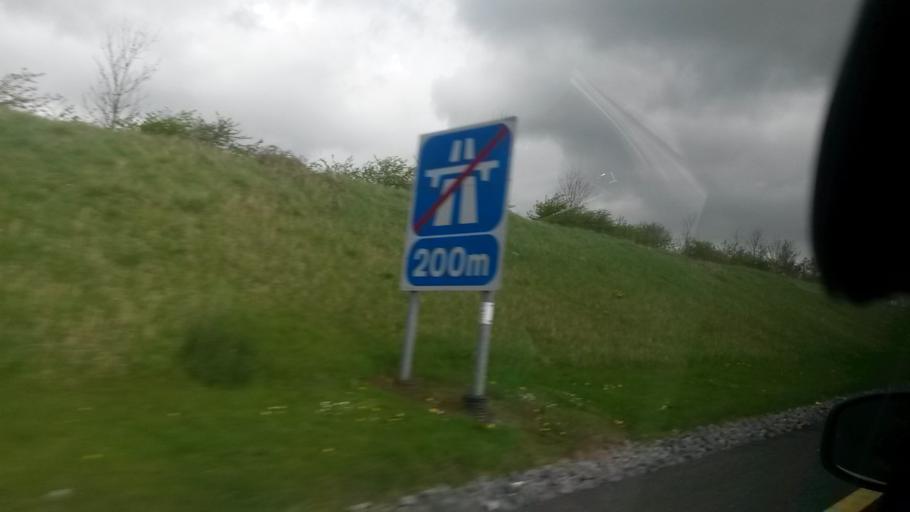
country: IE
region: Munster
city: Cashel
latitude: 52.4967
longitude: -7.8905
